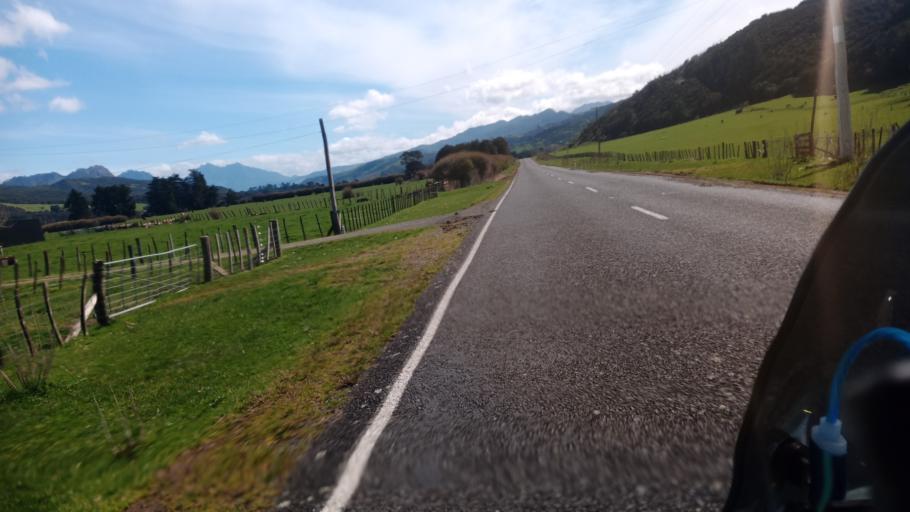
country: NZ
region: Gisborne
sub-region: Gisborne District
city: Gisborne
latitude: -37.8759
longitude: 178.2847
